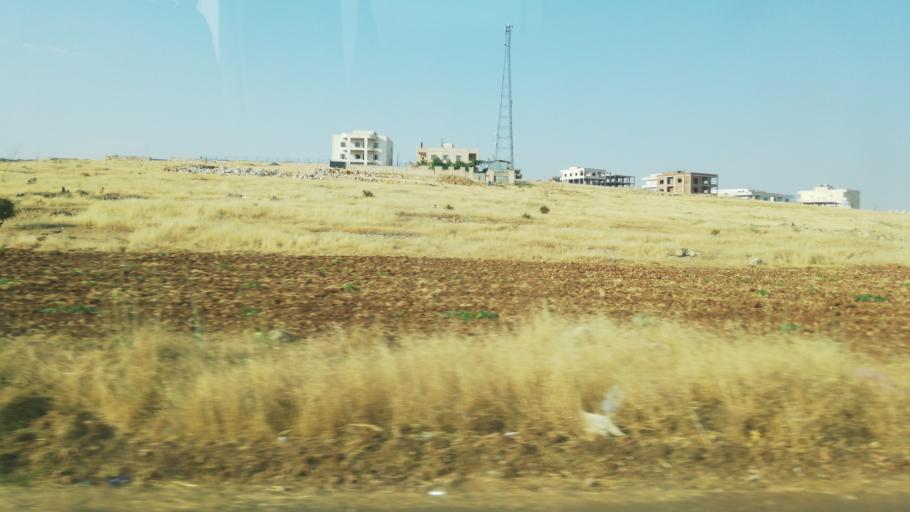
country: TR
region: Mardin
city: Acirli
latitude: 37.4416
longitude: 41.2907
